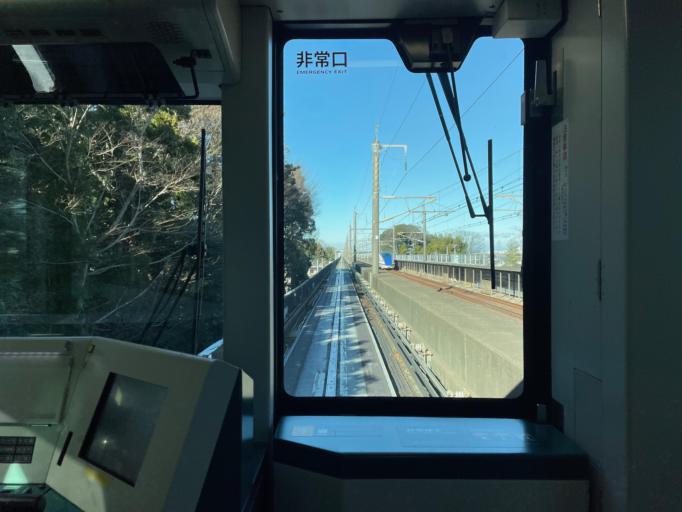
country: JP
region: Saitama
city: Ageoshimo
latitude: 36.0090
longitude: 139.6066
